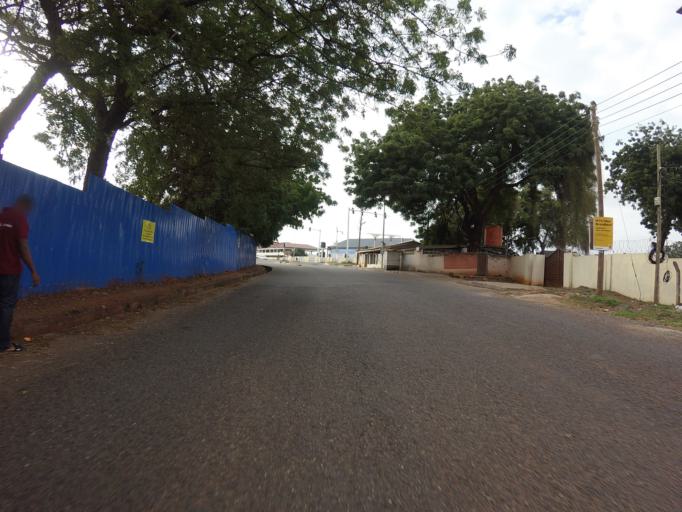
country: GH
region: Greater Accra
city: Accra
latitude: 5.5862
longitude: -0.1699
